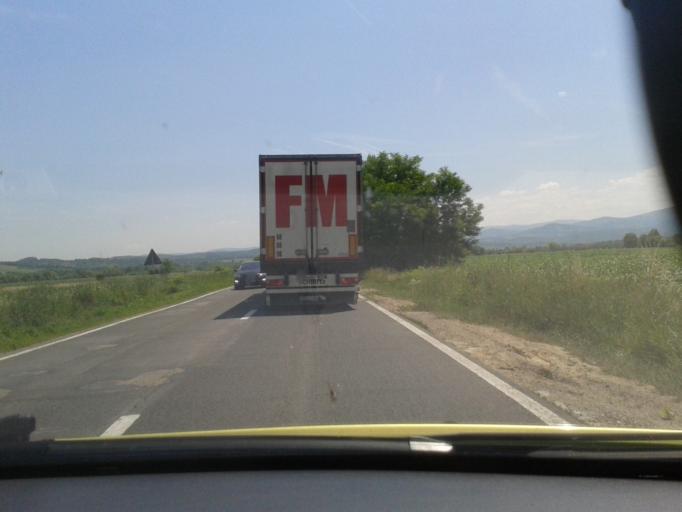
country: RO
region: Timis
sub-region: Comuna Margina
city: Margina
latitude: 45.8557
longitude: 22.2770
